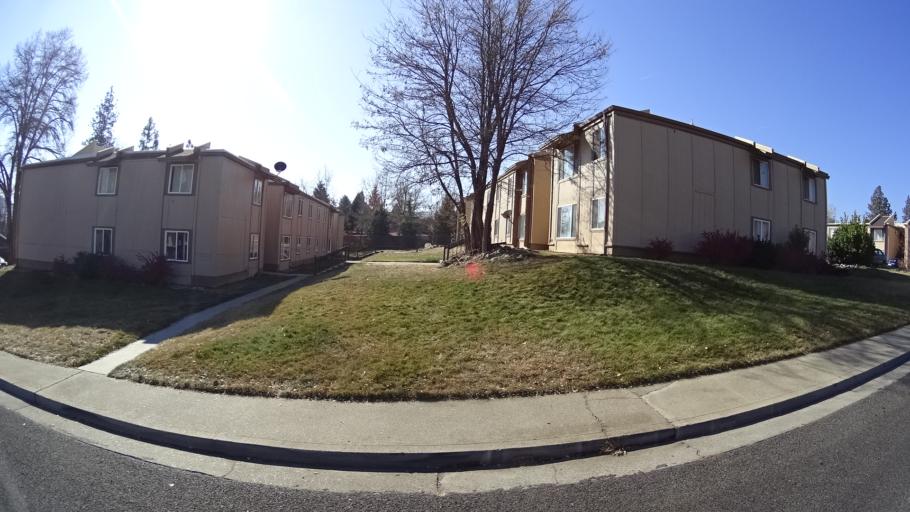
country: US
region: California
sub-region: Siskiyou County
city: Yreka
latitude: 41.7343
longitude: -122.6483
